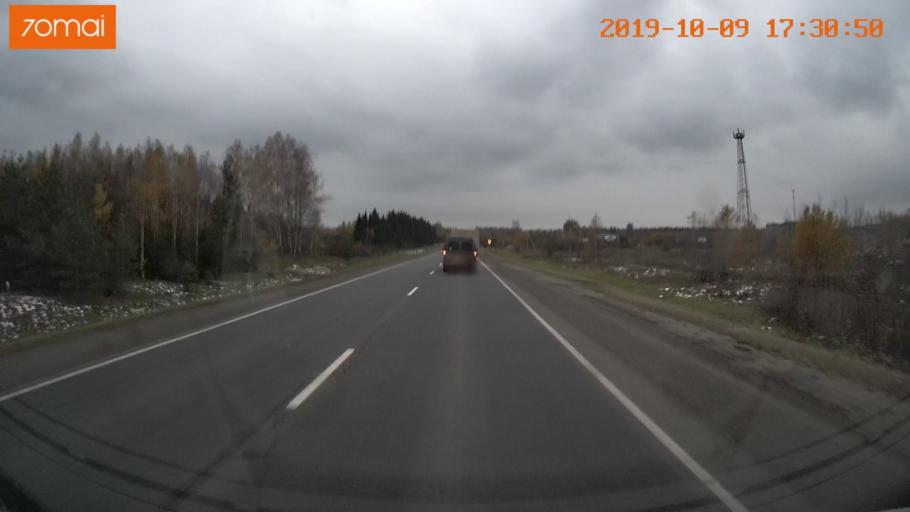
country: RU
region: Ivanovo
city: Bogorodskoye
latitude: 57.1398
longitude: 41.0453
